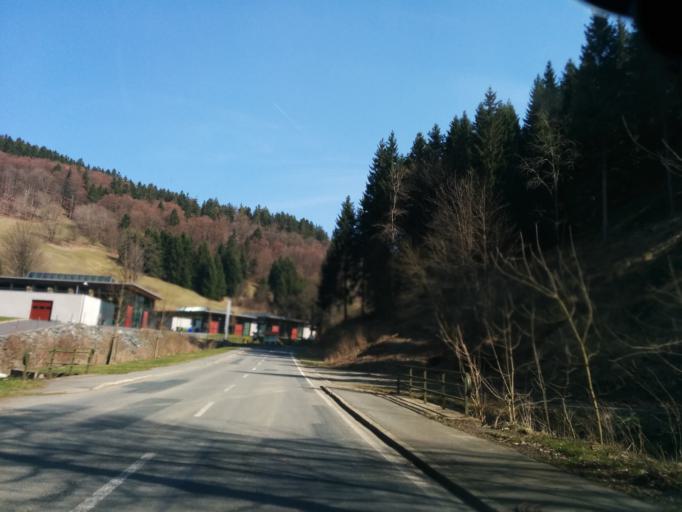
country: DE
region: Lower Saxony
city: Sankt Andreasberg
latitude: 51.7107
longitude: 10.4982
